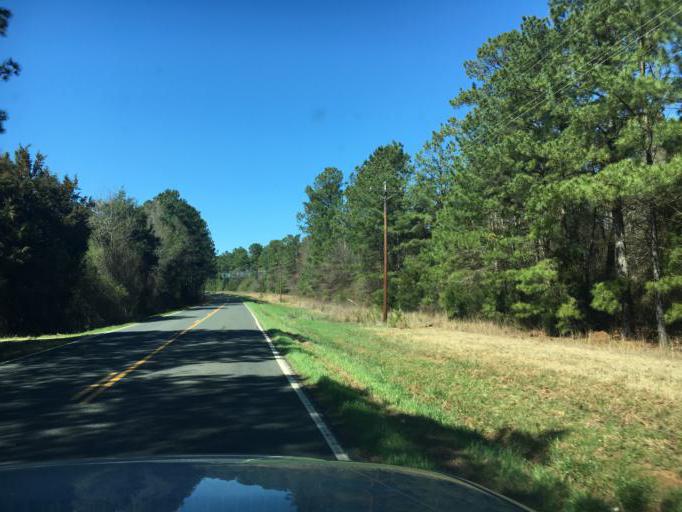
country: US
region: South Carolina
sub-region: Greenwood County
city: Ninety Six
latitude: 34.2875
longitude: -81.9580
